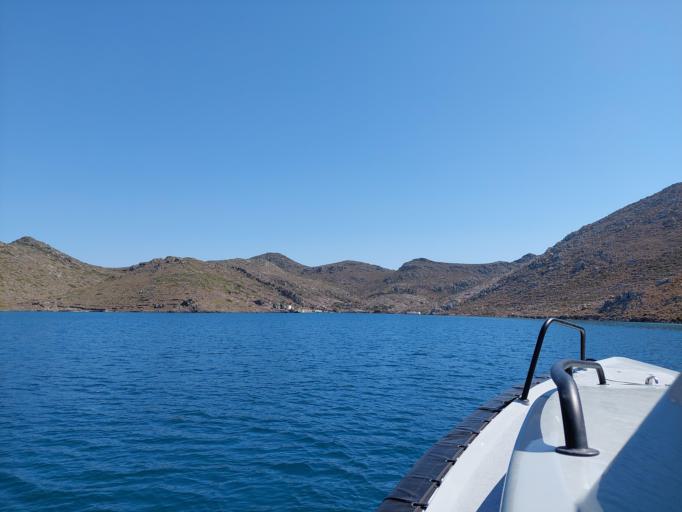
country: GR
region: South Aegean
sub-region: Nomos Dodekanisou
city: Karpathos
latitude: 35.8211
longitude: 27.2143
